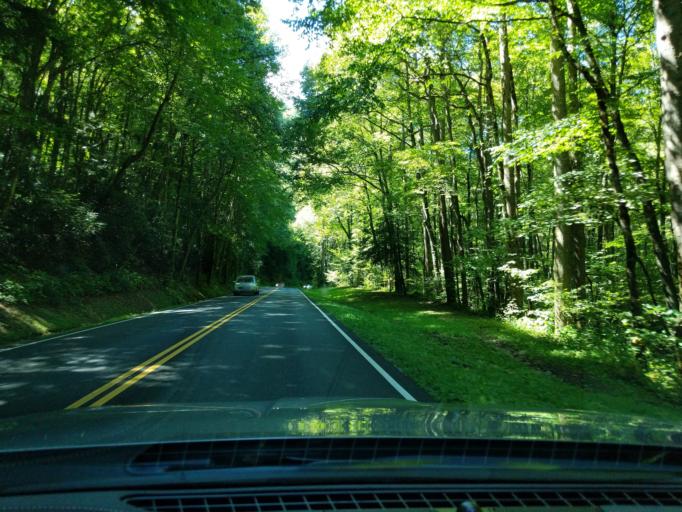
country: US
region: North Carolina
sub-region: Swain County
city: Cherokee
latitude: 35.5809
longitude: -83.3487
